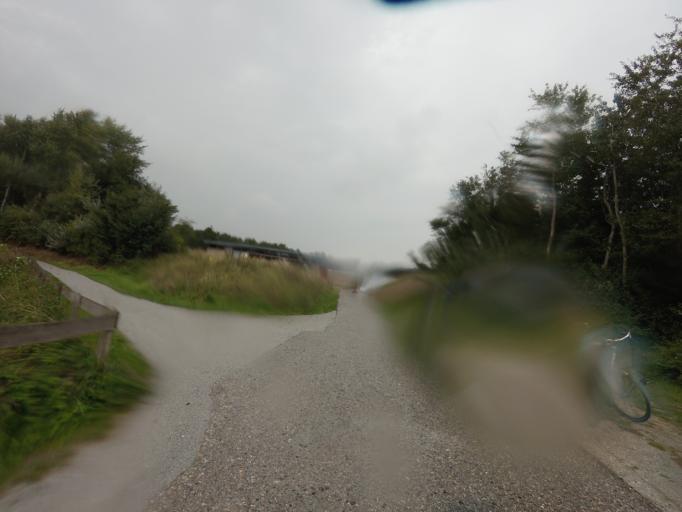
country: NL
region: Friesland
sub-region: Gemeente Schiermonnikoog
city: Schiermonnikoog
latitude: 53.4825
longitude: 6.1644
